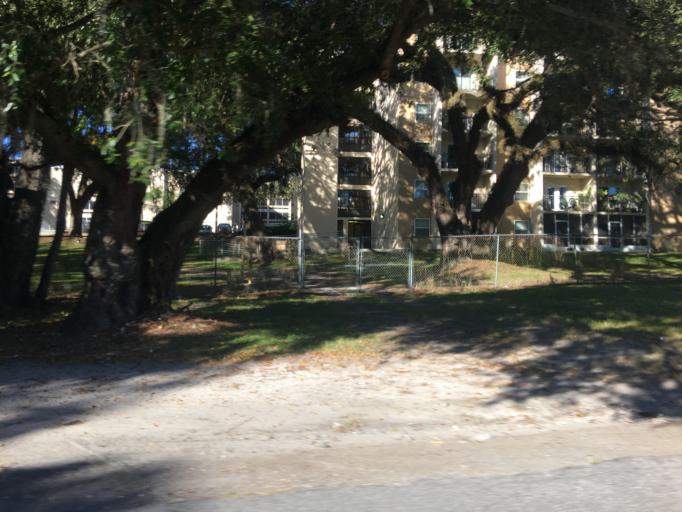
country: US
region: Florida
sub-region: Hillsborough County
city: Carrollwood
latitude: 28.0217
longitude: -82.4612
